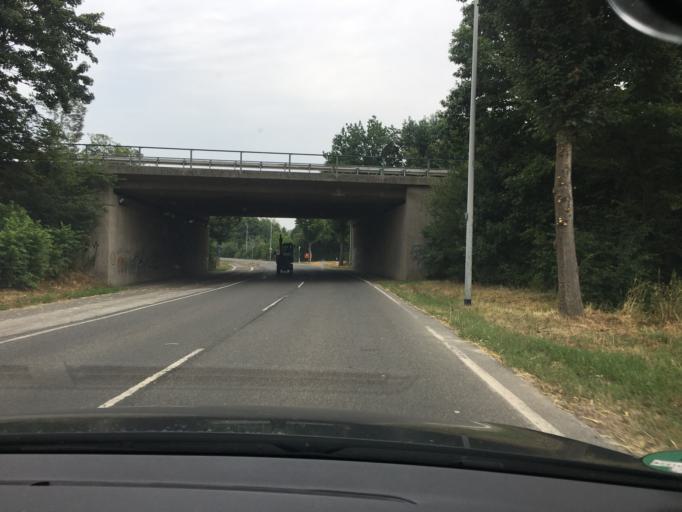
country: DE
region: North Rhine-Westphalia
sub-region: Regierungsbezirk Dusseldorf
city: Juchen
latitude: 51.1036
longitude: 6.4183
